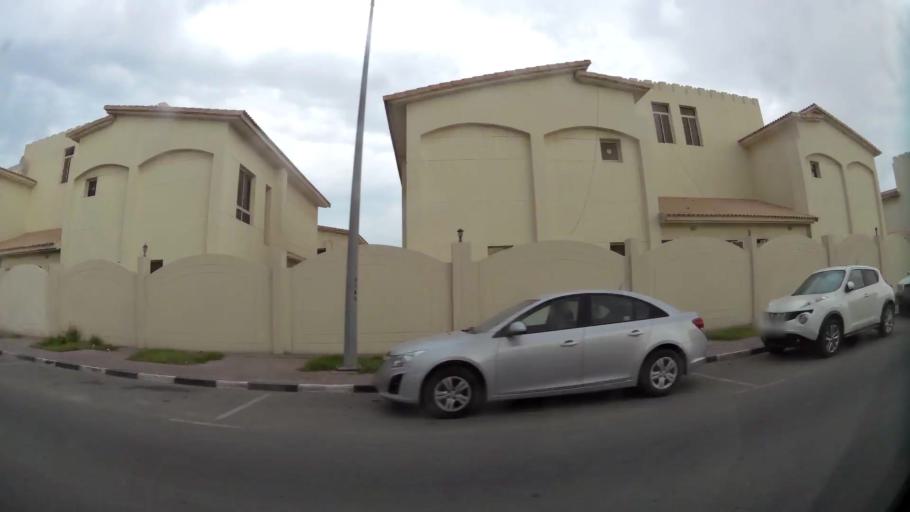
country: QA
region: Baladiyat ad Dawhah
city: Doha
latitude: 25.2706
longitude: 51.5000
